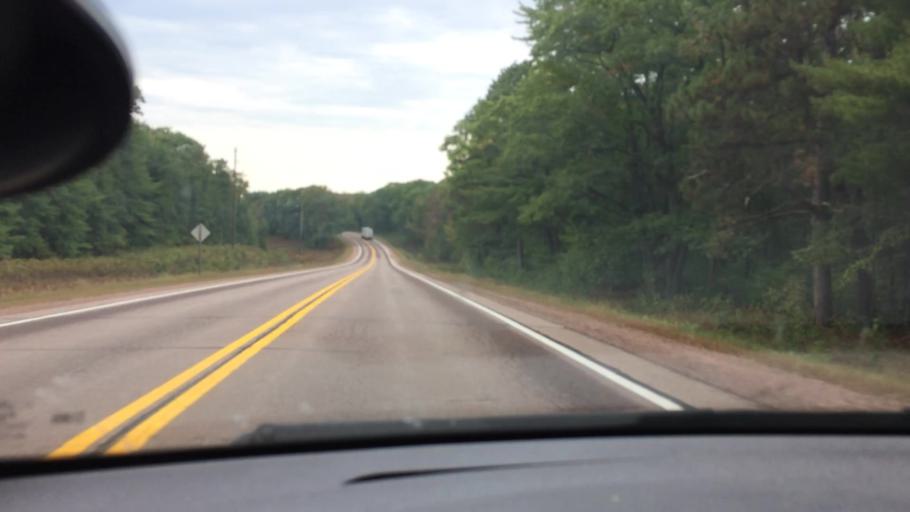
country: US
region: Wisconsin
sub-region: Clark County
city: Neillsville
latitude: 44.5826
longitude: -90.7434
